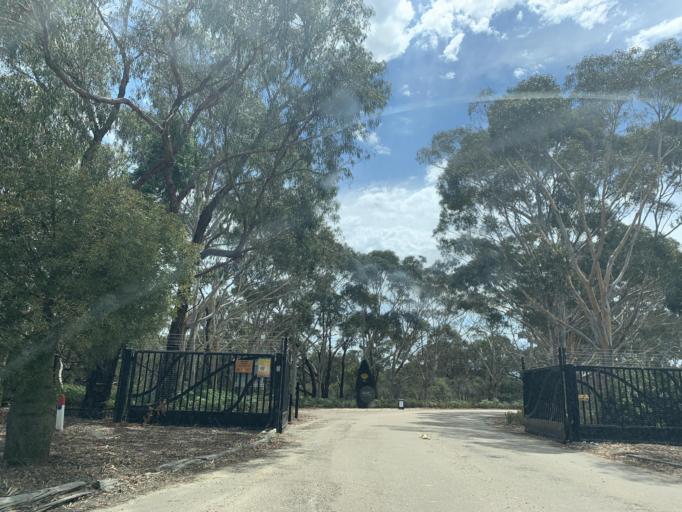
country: AU
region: Victoria
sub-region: Casey
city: Junction Village
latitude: -38.1285
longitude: 145.2862
